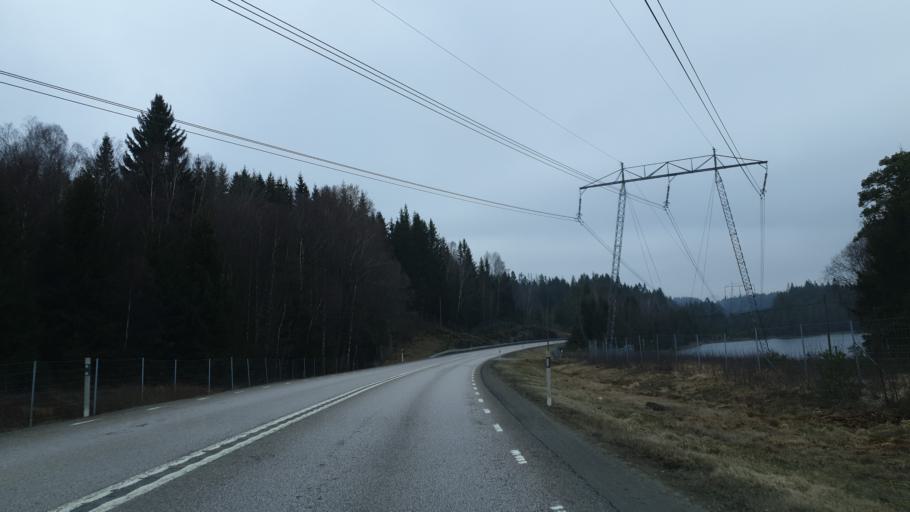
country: SE
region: Vaestra Goetaland
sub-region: Harryda Kommun
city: Hindas
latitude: 57.6397
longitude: 12.4059
